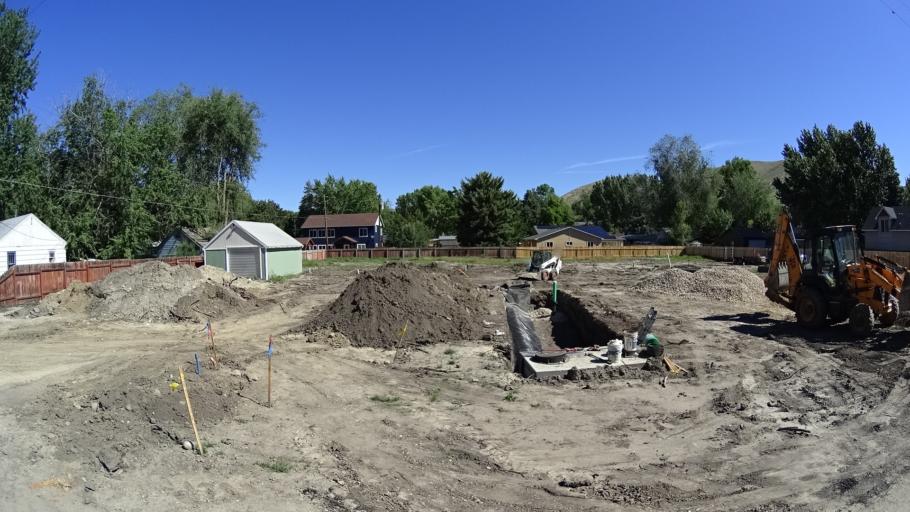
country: US
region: Idaho
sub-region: Ada County
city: Garden City
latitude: 43.6468
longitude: -116.2248
